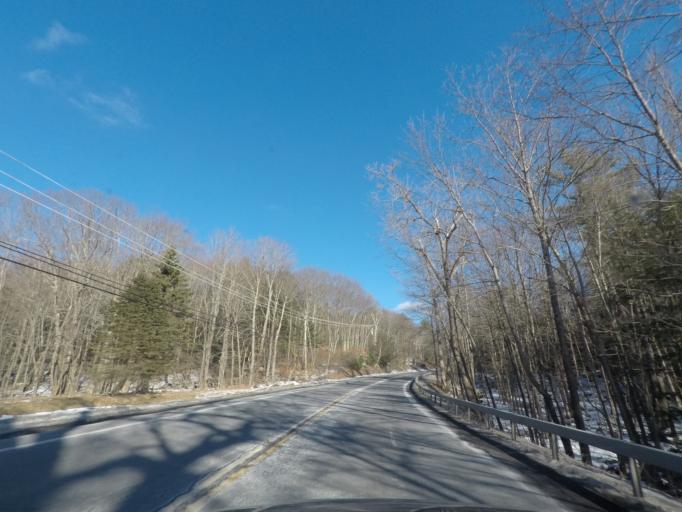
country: US
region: New York
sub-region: Columbia County
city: Chatham
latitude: 42.3197
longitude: -73.5121
